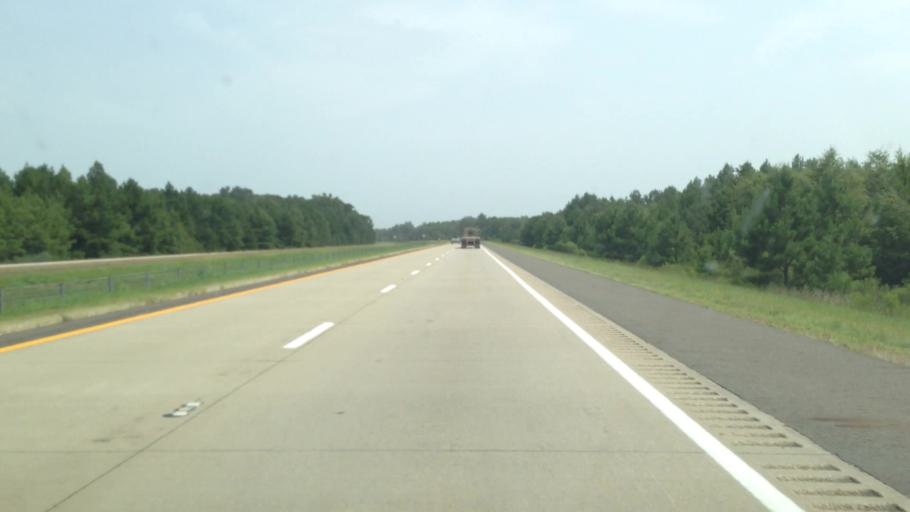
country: US
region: Texas
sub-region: Bowie County
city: Texarkana
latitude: 33.2061
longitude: -93.8757
